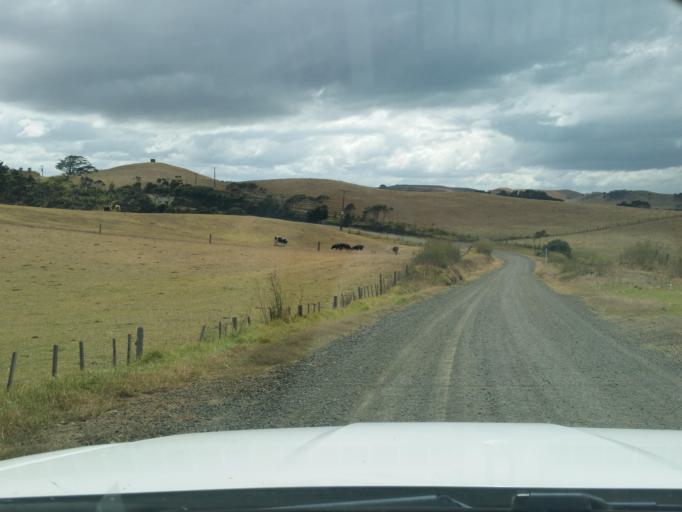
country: NZ
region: Auckland
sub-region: Auckland
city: Wellsford
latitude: -36.3513
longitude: 174.1716
